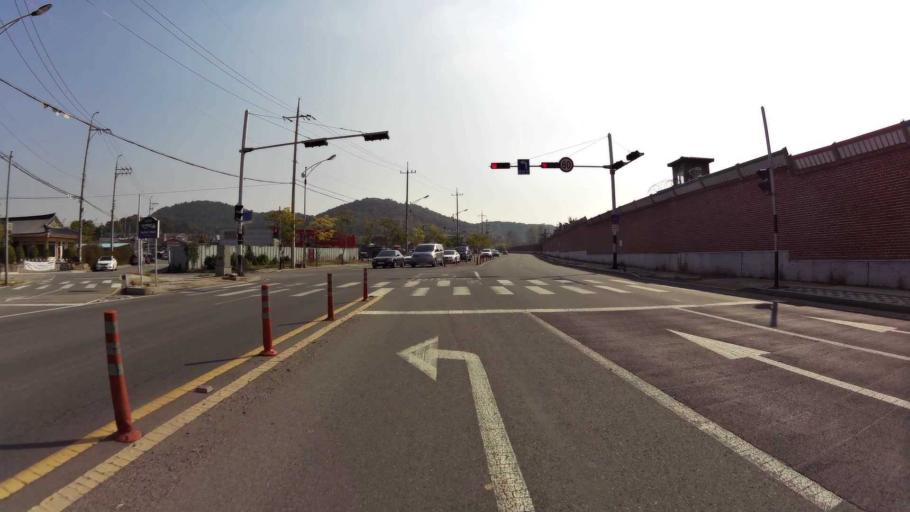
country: KR
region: Gyeongsangbuk-do
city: Gyeongsan-si
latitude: 35.8528
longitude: 128.6838
